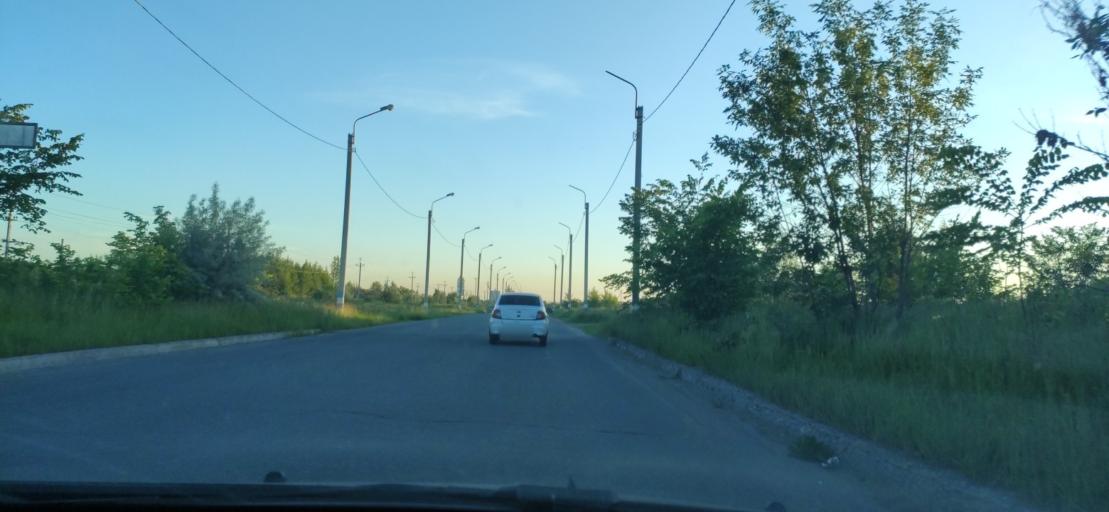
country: RU
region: Ulyanovsk
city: Mirnyy
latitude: 54.3789
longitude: 48.6707
